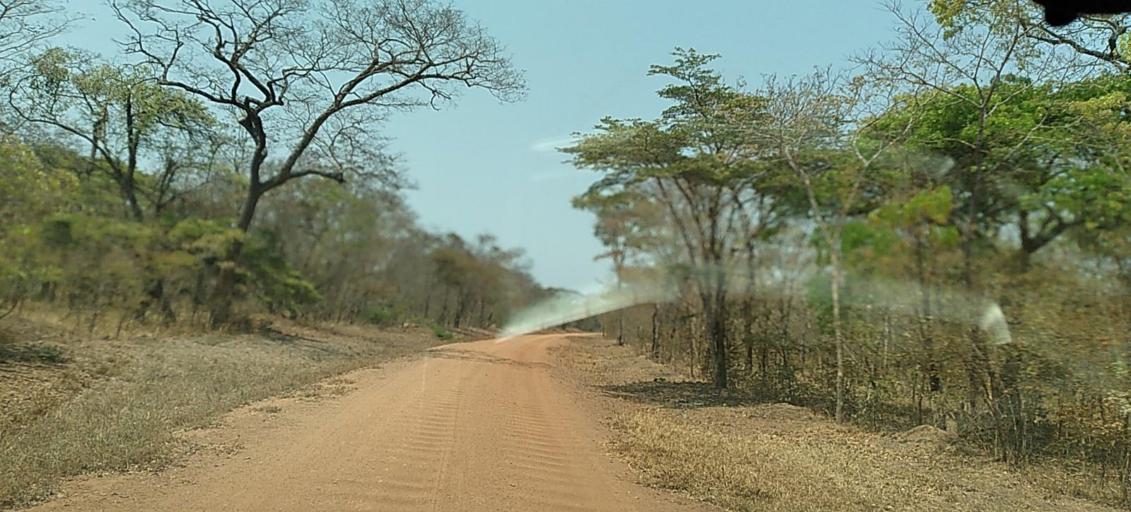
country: ZM
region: Central
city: Mumbwa
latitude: -14.2824
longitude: 26.5290
